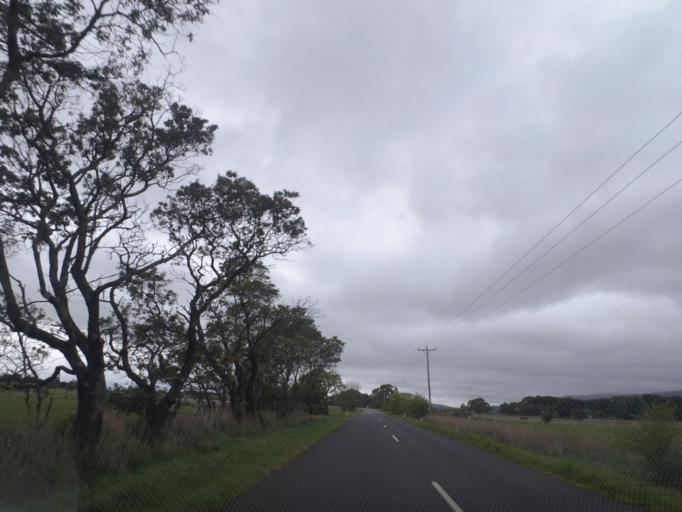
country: AU
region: Victoria
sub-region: Hume
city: Sunbury
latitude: -37.3247
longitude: 144.5544
